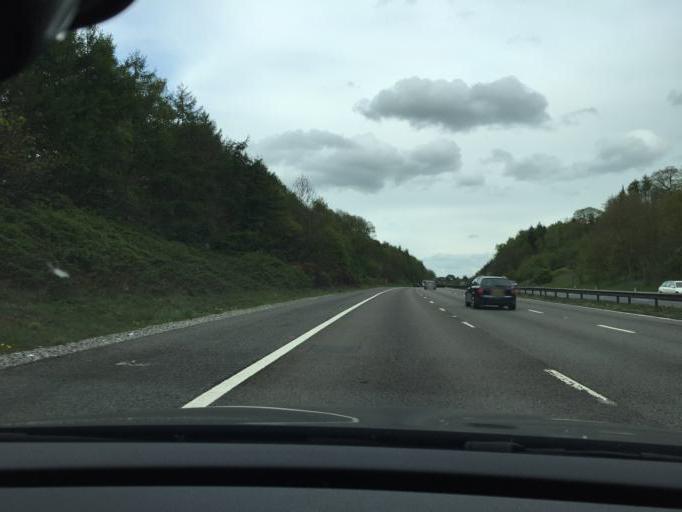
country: GB
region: England
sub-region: West Berkshire
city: Hermitage
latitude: 51.4621
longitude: -1.2126
